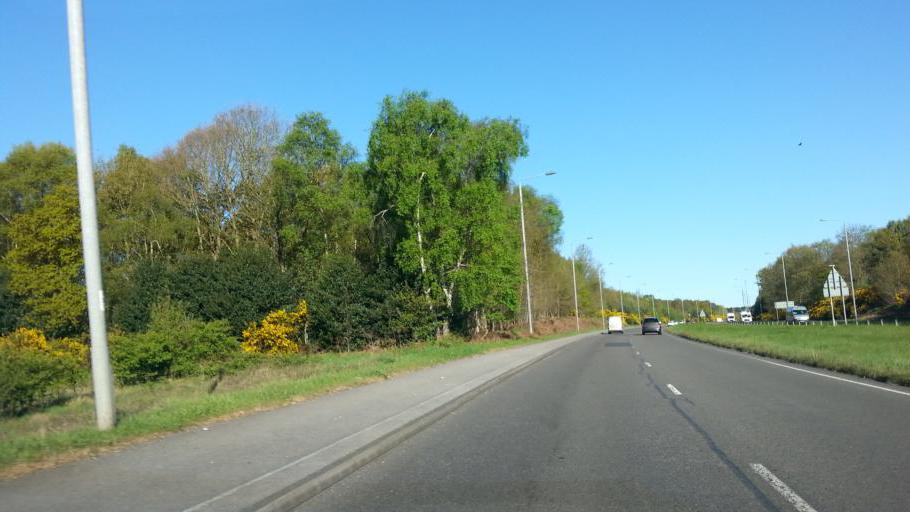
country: GB
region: England
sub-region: Nottinghamshire
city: Rainworth
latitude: 53.1230
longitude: -1.1189
